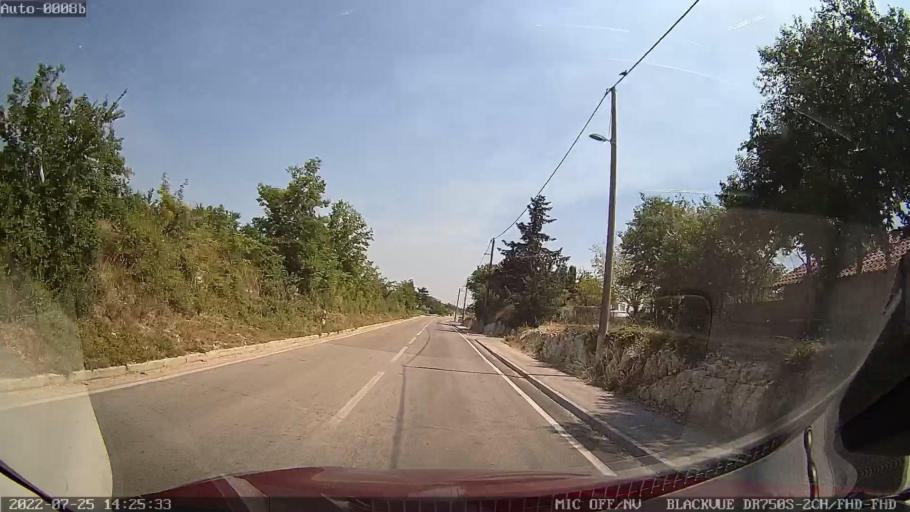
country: HR
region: Zadarska
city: Policnik
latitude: 44.1440
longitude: 15.3320
